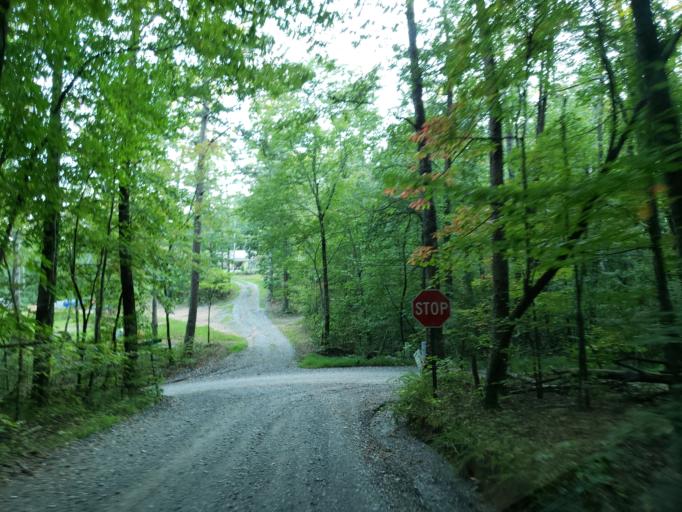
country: US
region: Georgia
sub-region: Fannin County
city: Blue Ridge
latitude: 34.6872
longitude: -84.2688
